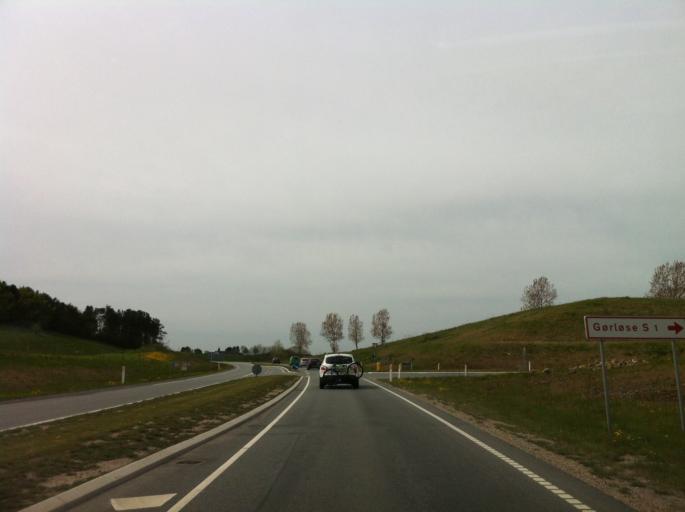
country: DK
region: Capital Region
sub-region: Frederikssund Kommune
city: Slangerup
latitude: 55.8770
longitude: 12.1973
